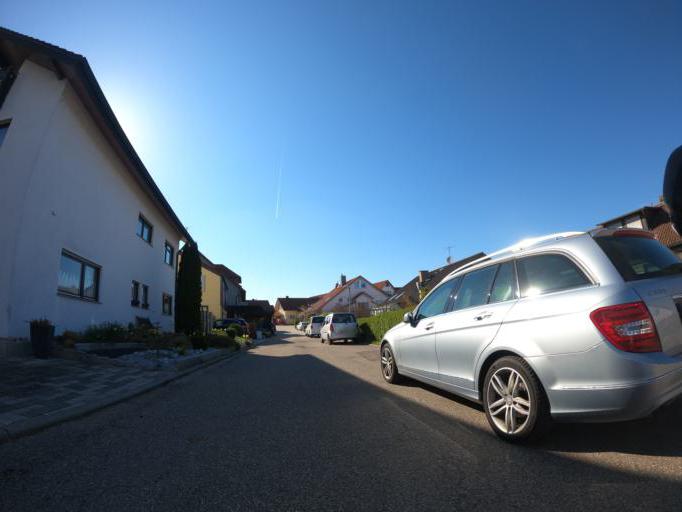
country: DE
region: Baden-Wuerttemberg
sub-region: Karlsruhe Region
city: Wimsheim
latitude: 48.8520
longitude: 8.8225
